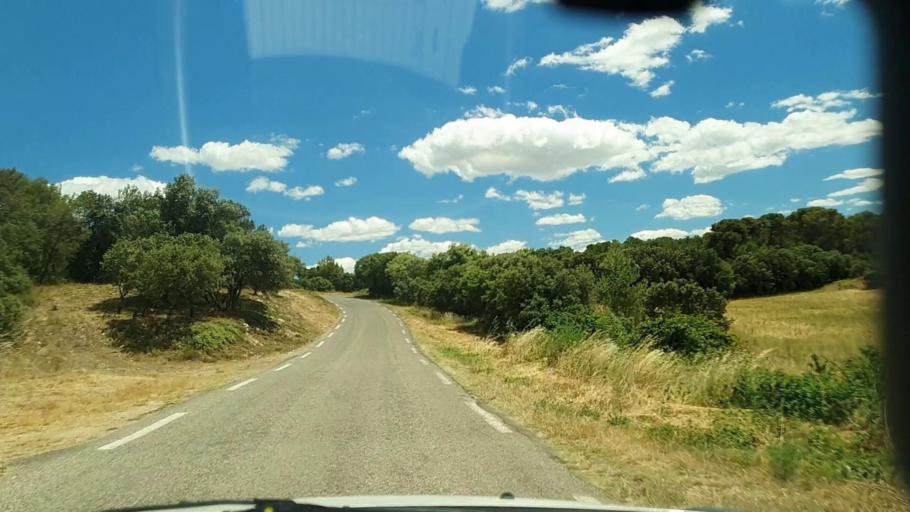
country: FR
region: Languedoc-Roussillon
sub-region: Departement du Gard
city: Cabrieres
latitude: 43.9099
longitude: 4.4512
